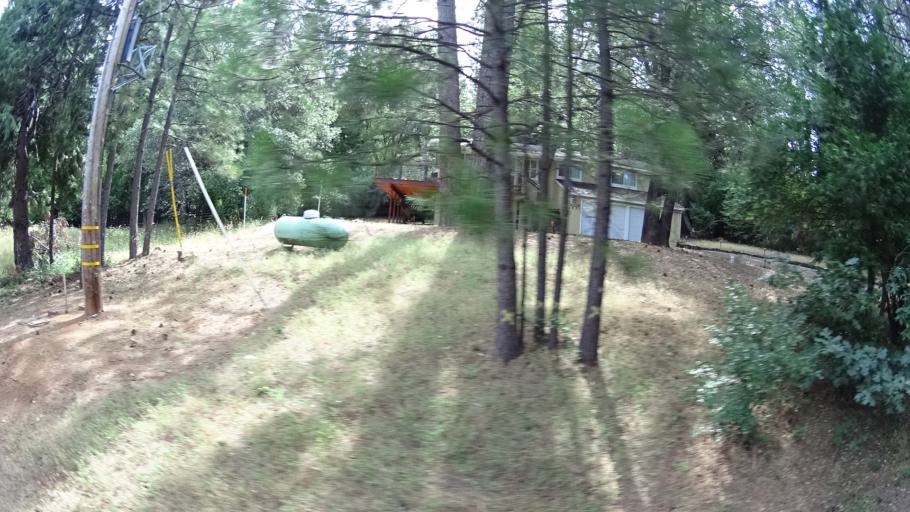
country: US
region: California
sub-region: Calaveras County
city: Arnold
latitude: 38.2452
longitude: -120.3591
